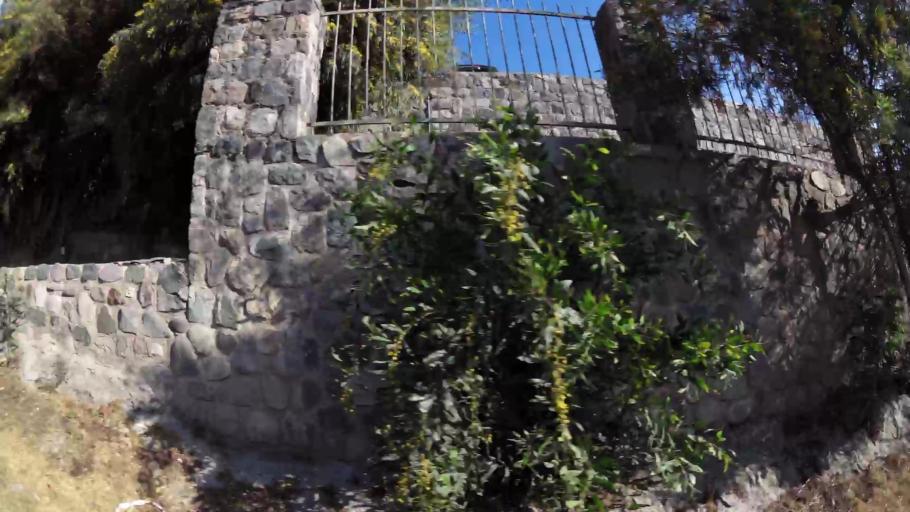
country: CL
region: Santiago Metropolitan
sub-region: Provincia de Santiago
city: Villa Presidente Frei, Nunoa, Santiago, Chile
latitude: -33.3646
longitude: -70.4902
